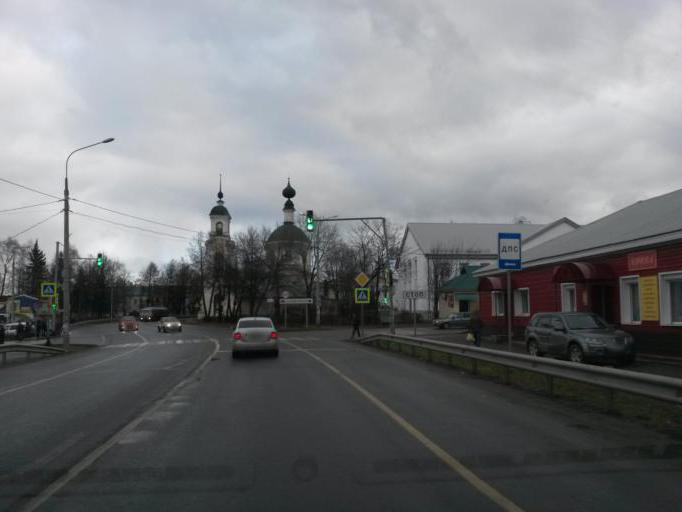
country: RU
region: Jaroslavl
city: Petrovsk
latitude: 57.0126
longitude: 39.2630
